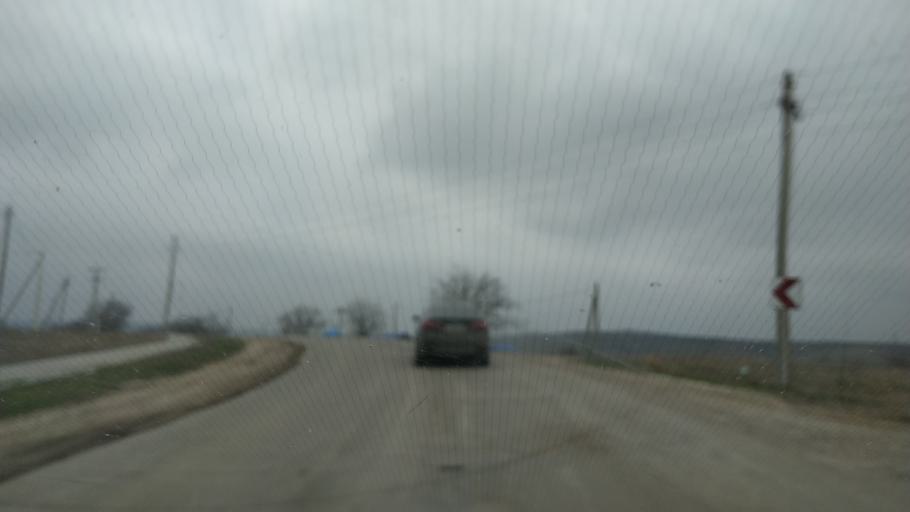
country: MD
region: Gagauzia
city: Comrat
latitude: 46.2843
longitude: 28.6750
